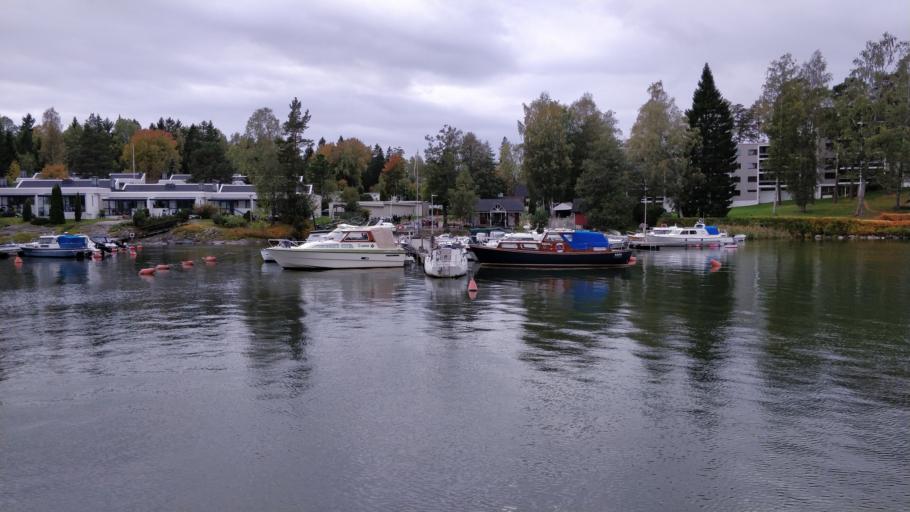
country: FI
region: Uusimaa
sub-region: Helsinki
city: Vantaa
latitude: 60.1808
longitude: 25.0662
